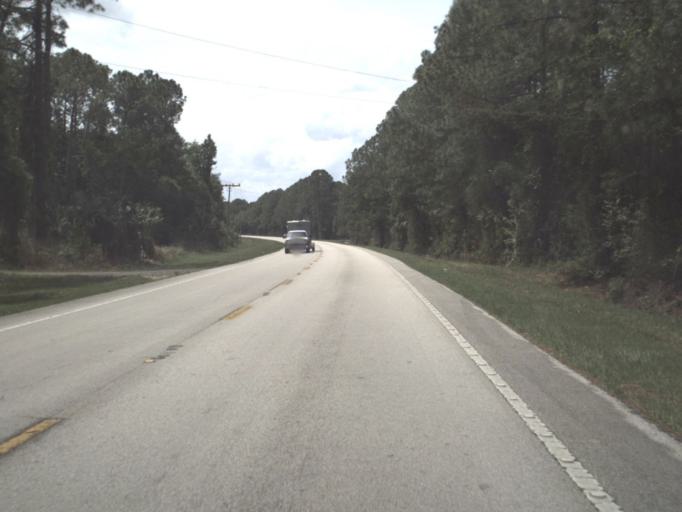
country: US
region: Florida
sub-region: Lake County
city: Lake Mack-Forest Hills
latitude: 29.0017
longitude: -81.3902
